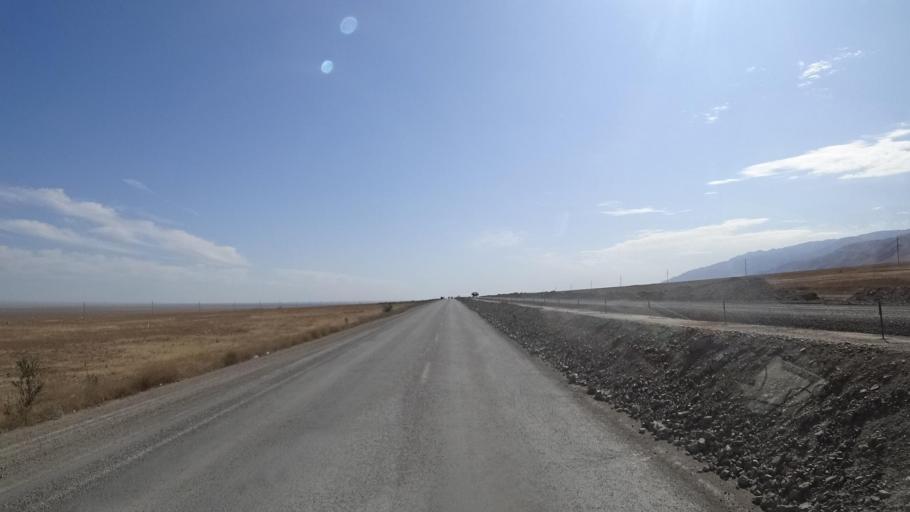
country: KG
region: Chuy
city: Ivanovka
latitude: 43.3841
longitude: 75.1761
